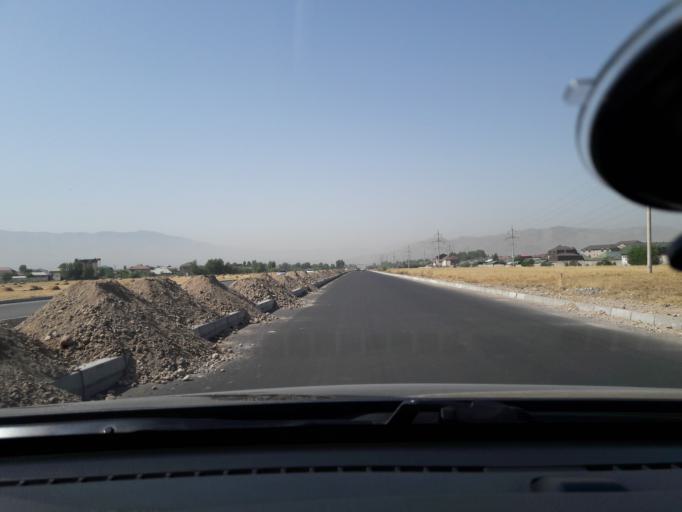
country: TJ
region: Dushanbe
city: Dushanbe
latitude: 38.4963
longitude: 68.7542
